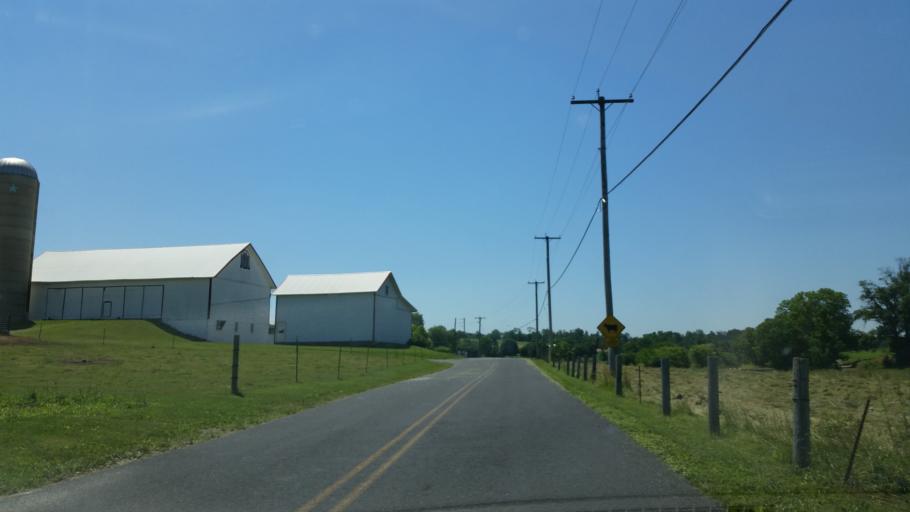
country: US
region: Pennsylvania
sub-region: Lebanon County
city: Fredericksburg
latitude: 40.4293
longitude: -76.4311
